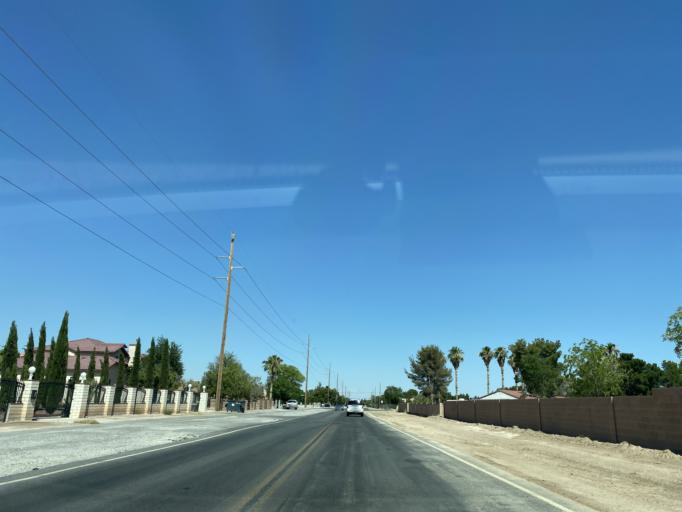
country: US
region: Nevada
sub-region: Clark County
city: Las Vegas
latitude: 36.2691
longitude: -115.2356
